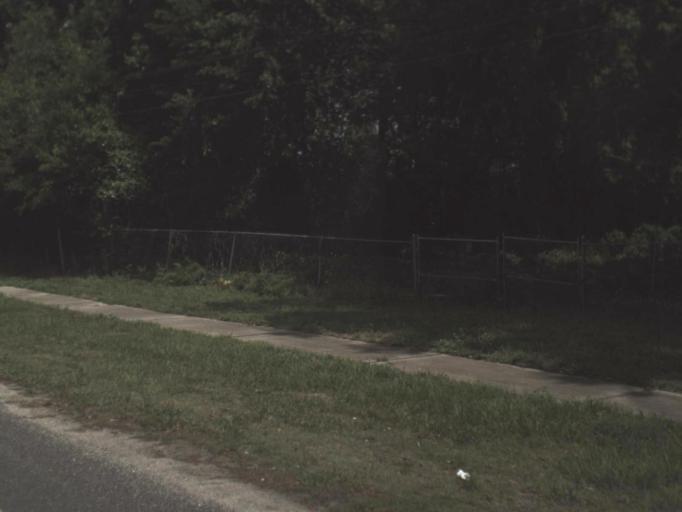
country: US
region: Florida
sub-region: Saint Johns County
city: Fruit Cove
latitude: 30.1463
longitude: -81.5207
